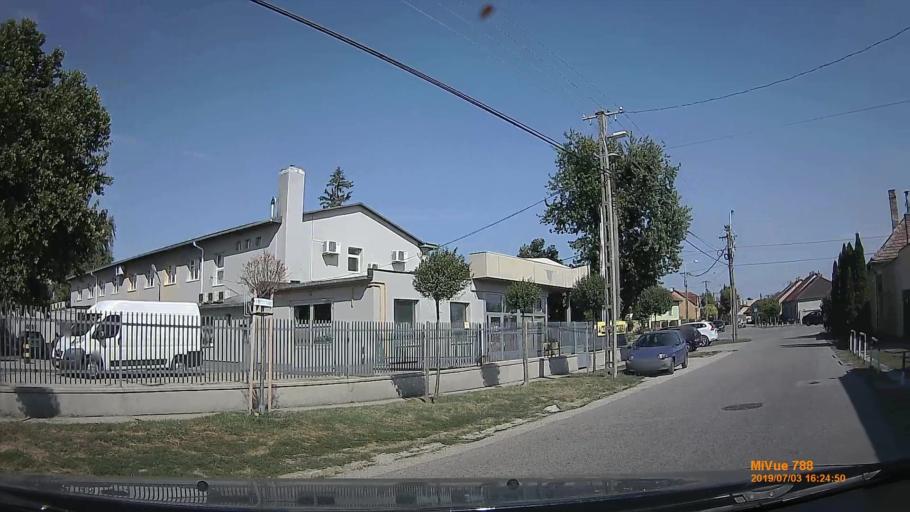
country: HU
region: Gyor-Moson-Sopron
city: Gyor
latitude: 47.6841
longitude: 17.6035
